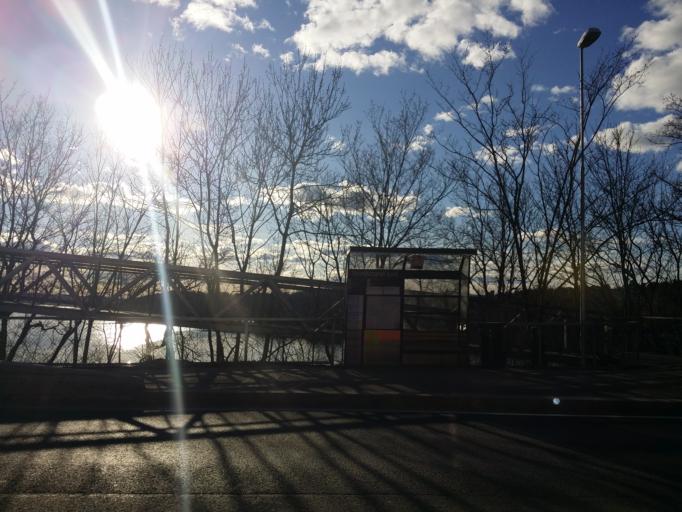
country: NO
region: Oslo
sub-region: Oslo
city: Oslo
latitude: 59.8670
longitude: 10.7831
